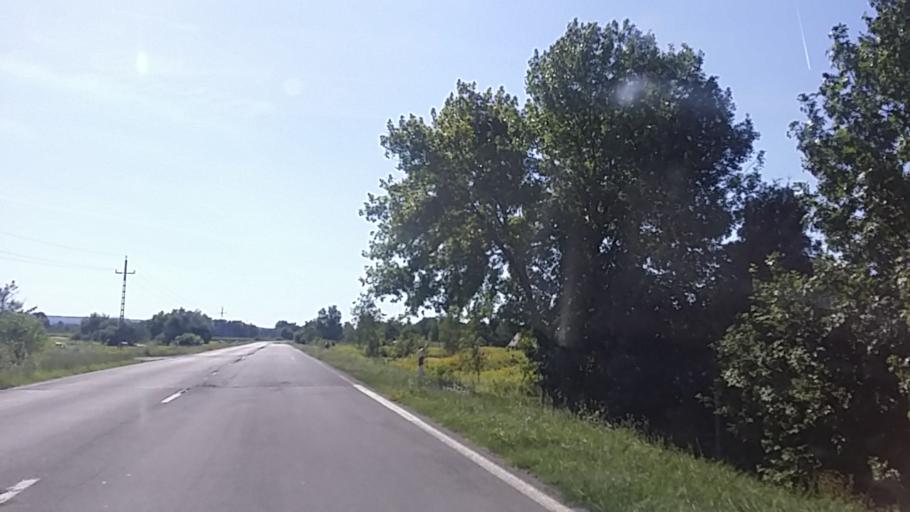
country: HU
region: Somogy
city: Kethely
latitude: 46.6983
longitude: 17.4211
